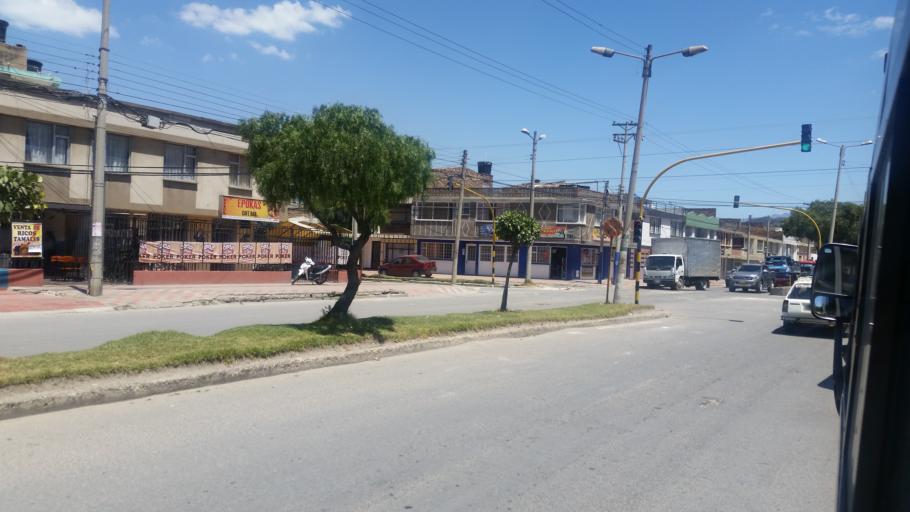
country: CO
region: Boyaca
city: Sogamoso
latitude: 5.7225
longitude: -72.9307
